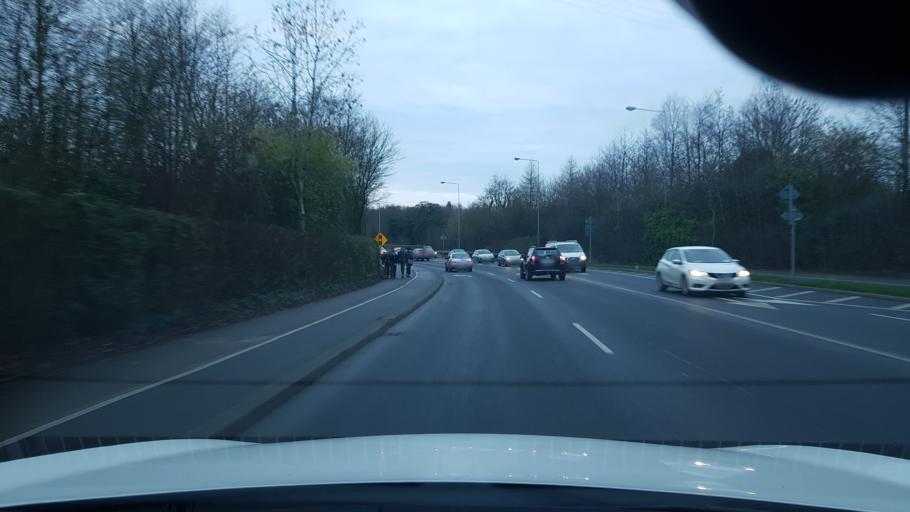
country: IE
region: Leinster
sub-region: An Mhi
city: Navan
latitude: 53.6578
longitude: -6.6858
